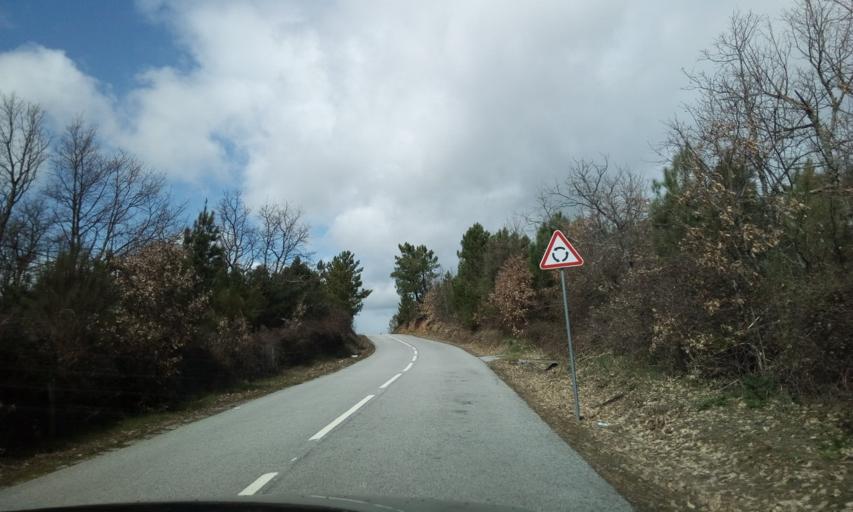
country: PT
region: Guarda
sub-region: Fornos de Algodres
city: Fornos de Algodres
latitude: 40.6372
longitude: -7.5475
